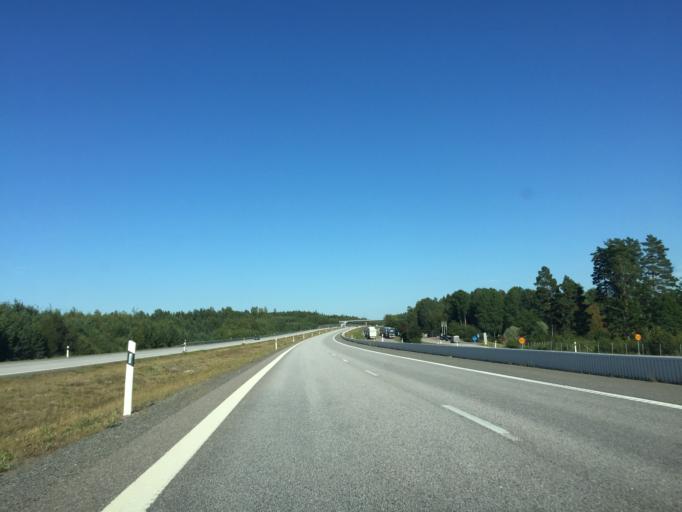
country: SE
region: Vaestmanland
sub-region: Arboga Kommun
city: Arboga
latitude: 59.3977
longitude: 15.7095
